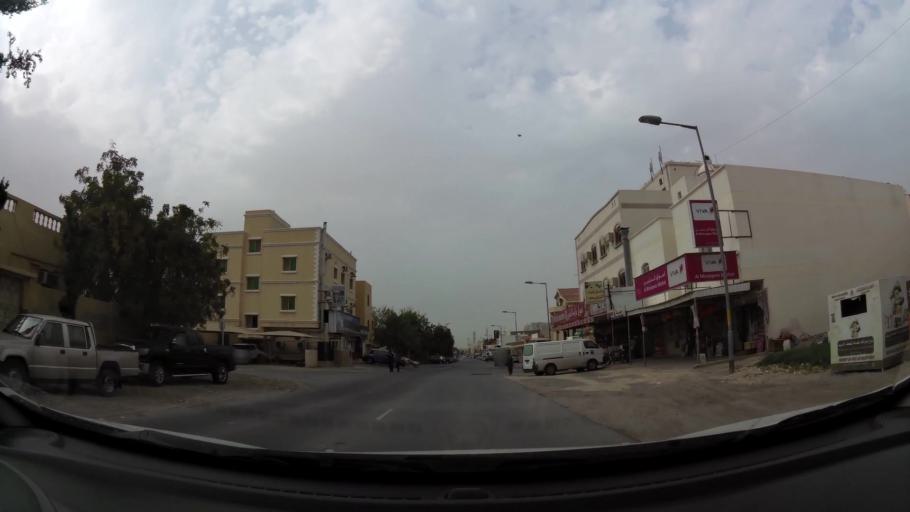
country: BH
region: Northern
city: Ar Rifa'
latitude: 26.1218
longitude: 50.5796
